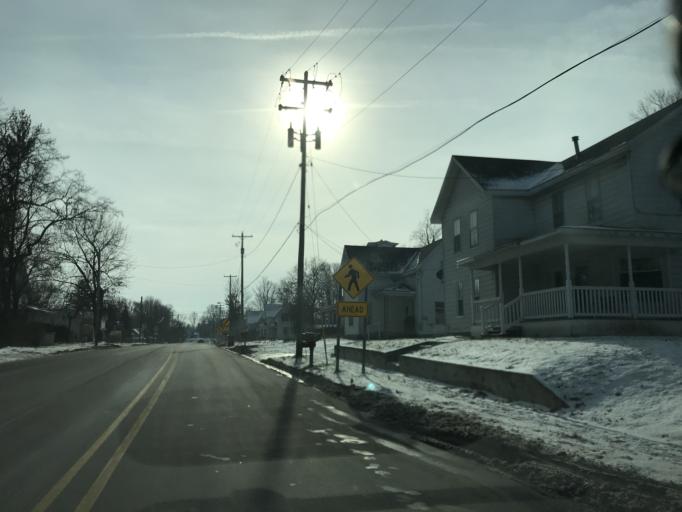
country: US
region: Michigan
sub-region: Barry County
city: Nashville
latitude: 42.5998
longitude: -85.0937
